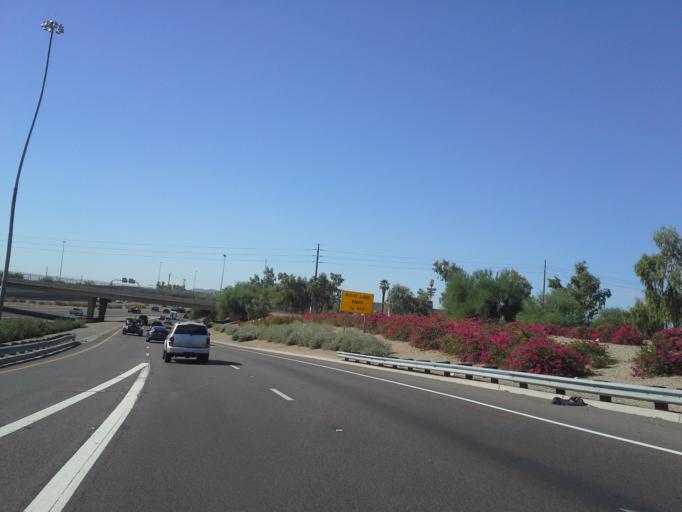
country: US
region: Arizona
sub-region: Maricopa County
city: Phoenix
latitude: 33.4602
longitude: -112.0383
